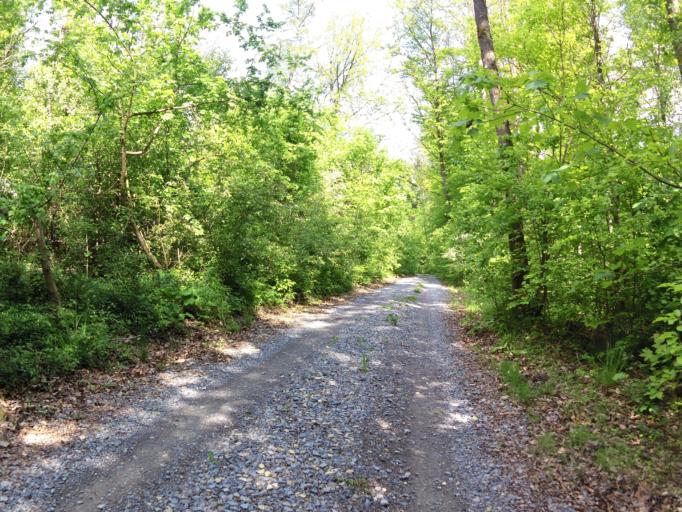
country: DE
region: Bavaria
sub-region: Regierungsbezirk Unterfranken
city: Reichenberg
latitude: 49.7359
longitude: 9.8877
